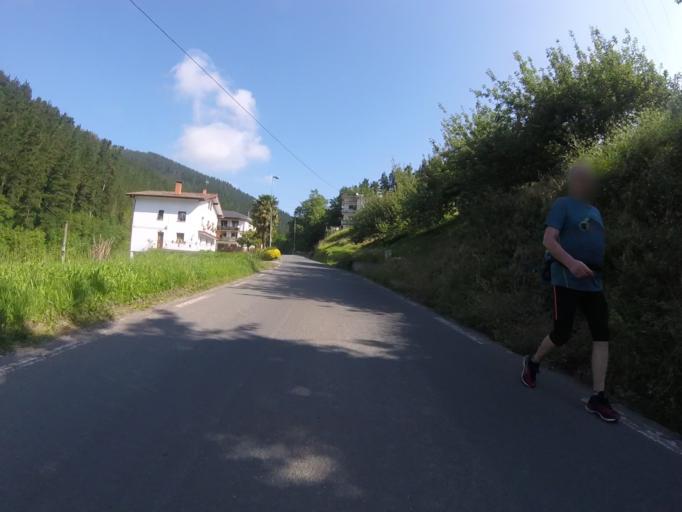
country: ES
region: Basque Country
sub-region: Provincia de Guipuzcoa
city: Ormaiztegui
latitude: 43.0604
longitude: -2.2380
